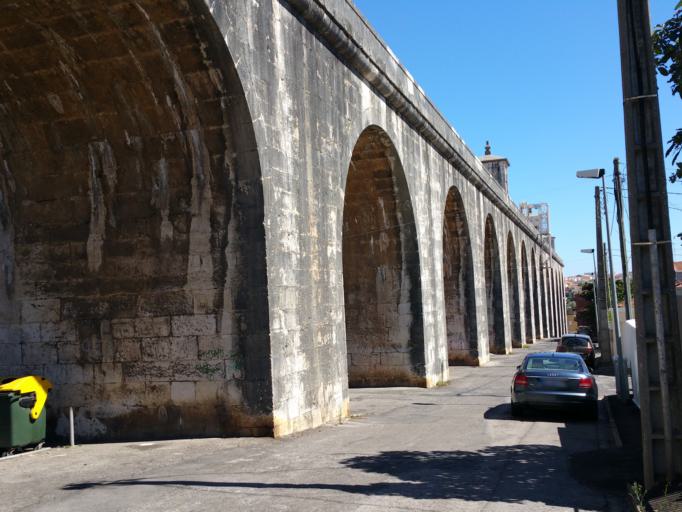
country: PT
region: Lisbon
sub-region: Lisbon
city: Lisbon
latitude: 38.7324
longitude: -9.1722
